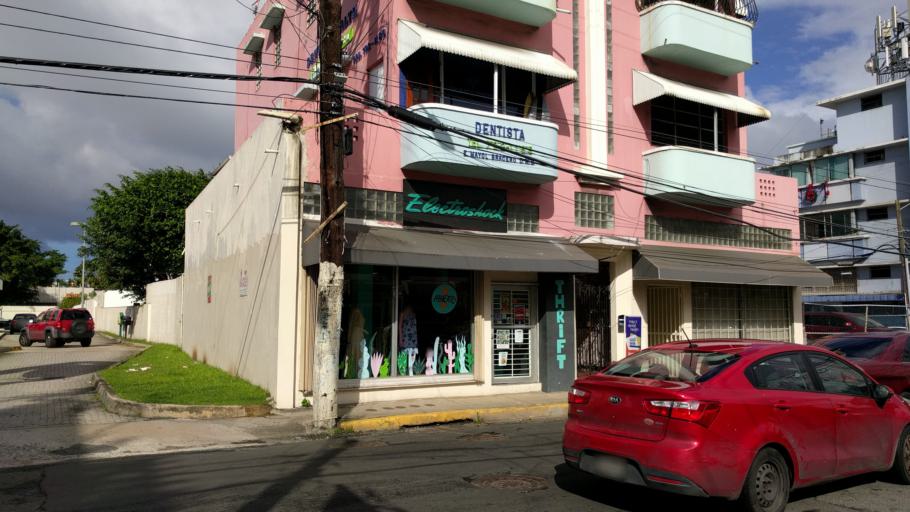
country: PR
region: San Juan
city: San Juan
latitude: 18.4513
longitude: -66.0587
